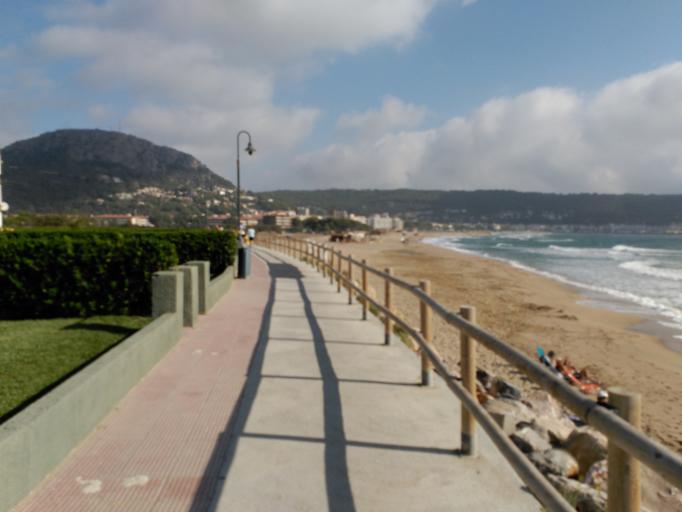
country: ES
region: Catalonia
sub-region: Provincia de Girona
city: Torroella de Montgri
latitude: 42.0429
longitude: 3.1964
